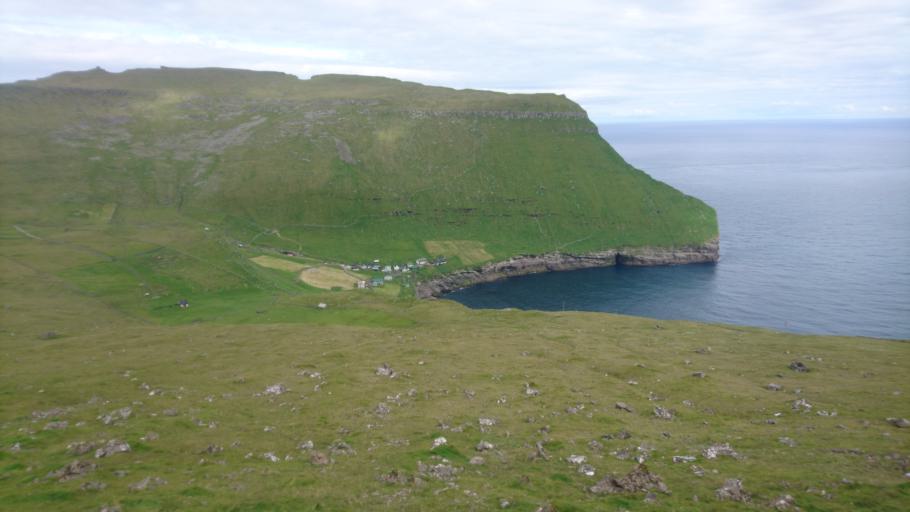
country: FO
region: Nordoyar
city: Klaksvik
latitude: 62.3249
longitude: -6.2872
